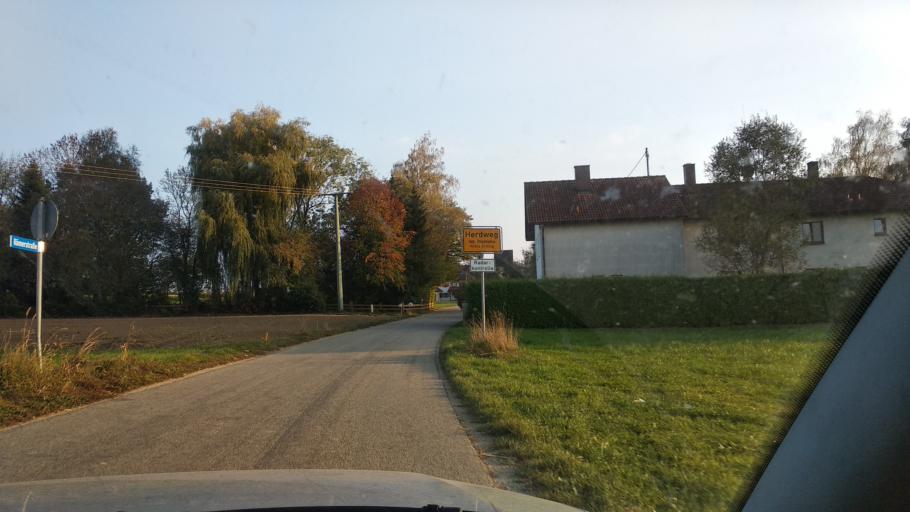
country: DE
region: Bavaria
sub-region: Upper Bavaria
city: Ottenhofen
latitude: 48.2026
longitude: 11.8942
